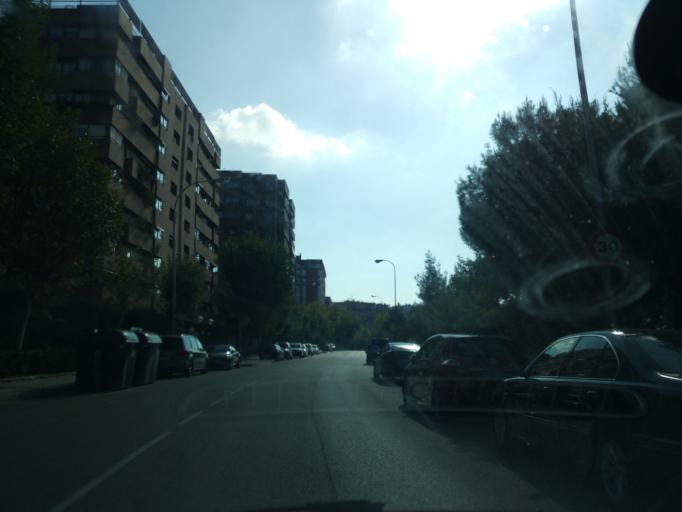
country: ES
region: Madrid
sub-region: Provincia de Madrid
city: Fuencarral-El Pardo
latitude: 40.4838
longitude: -3.7360
